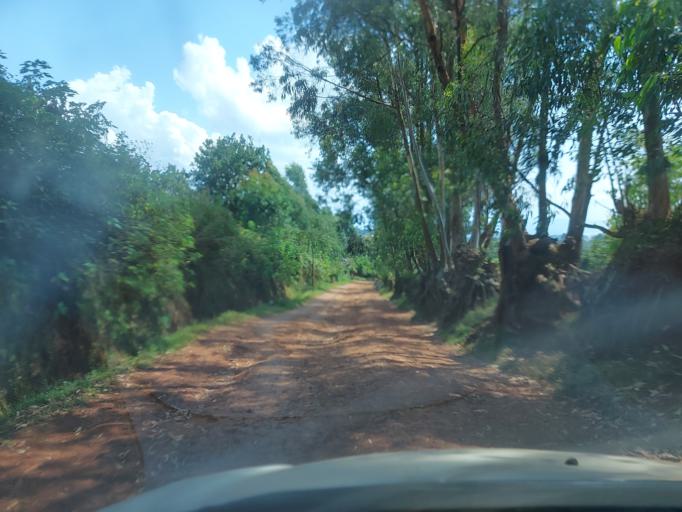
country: CD
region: South Kivu
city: Bukavu
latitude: -2.5044
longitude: 28.8257
